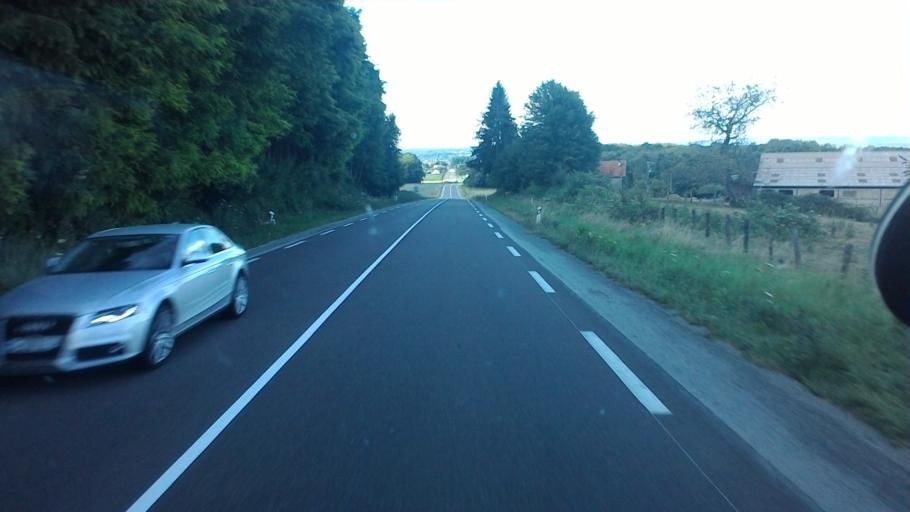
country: FR
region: Franche-Comte
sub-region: Departement de la Haute-Saone
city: Luxeuil-les-Bains
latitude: 47.7613
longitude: 6.3397
